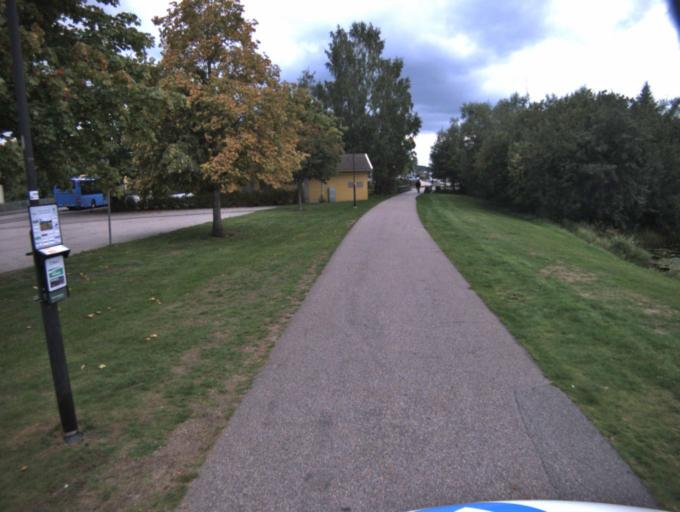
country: SE
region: Vaestra Goetaland
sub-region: Ulricehamns Kommun
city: Ulricehamn
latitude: 57.8004
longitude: 13.4122
